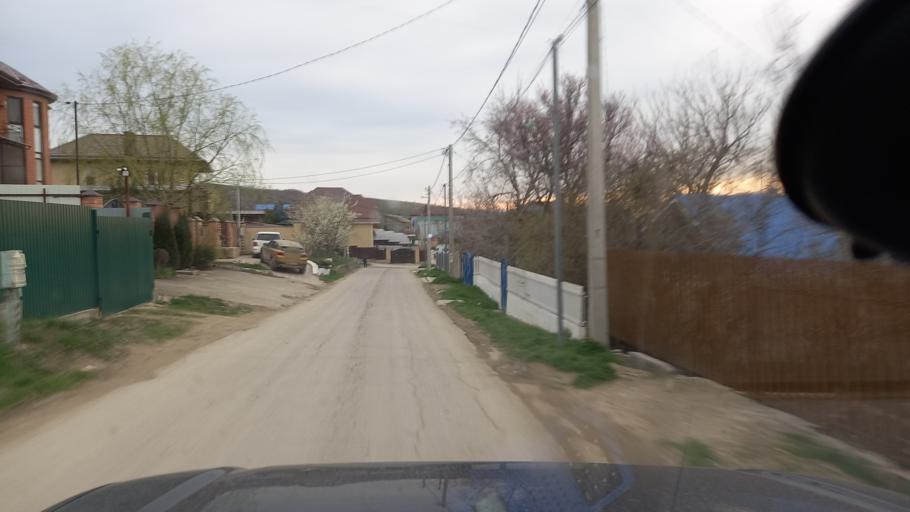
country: RU
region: Krasnodarskiy
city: Anapa
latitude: 44.8504
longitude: 37.3524
